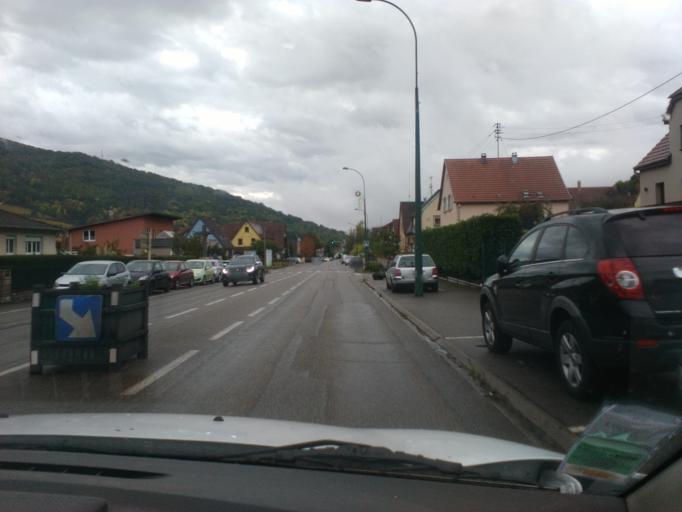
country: FR
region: Alsace
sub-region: Departement du Haut-Rhin
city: Kaysersberg
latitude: 48.1491
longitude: 7.2490
